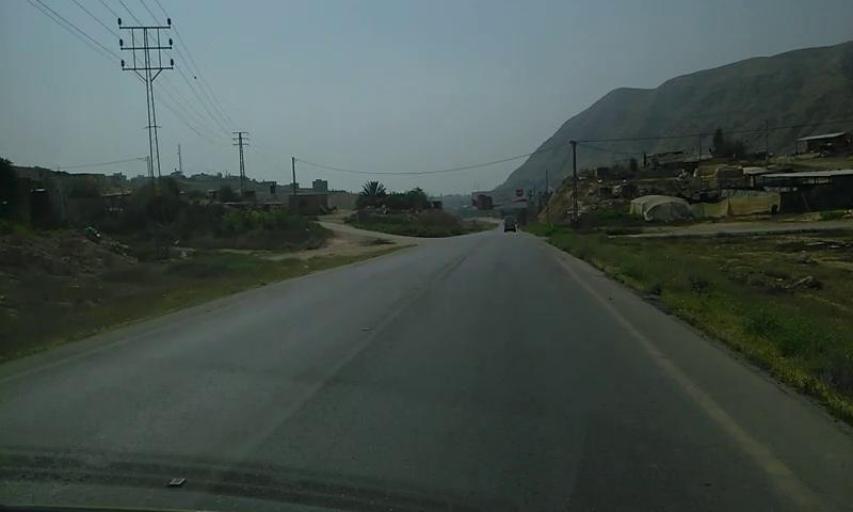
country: PS
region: West Bank
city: An Nuway`imah
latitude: 31.8959
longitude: 35.4284
